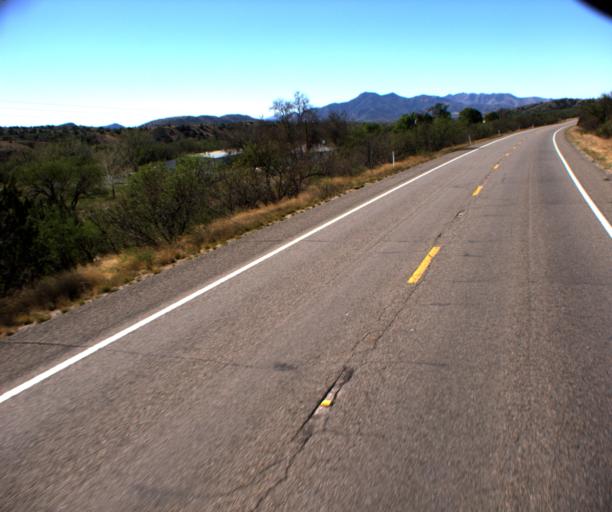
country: US
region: Arizona
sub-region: Santa Cruz County
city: Rio Rico
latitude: 31.6271
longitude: -110.7154
